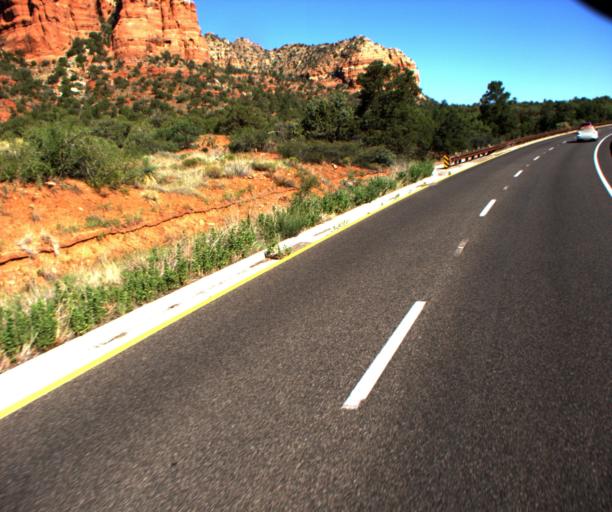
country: US
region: Arizona
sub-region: Yavapai County
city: Village of Oak Creek (Big Park)
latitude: 34.7995
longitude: -111.7678
